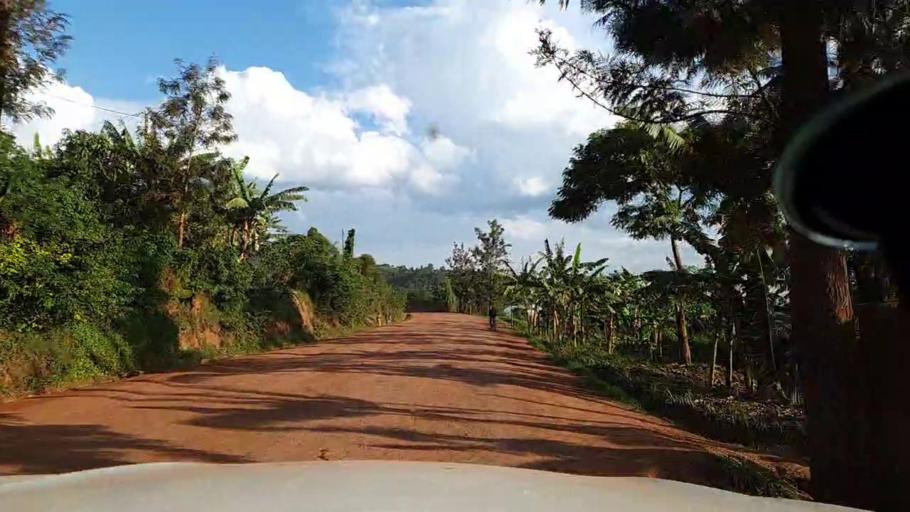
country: RW
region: Kigali
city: Kigali
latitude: -1.9142
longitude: 29.9859
